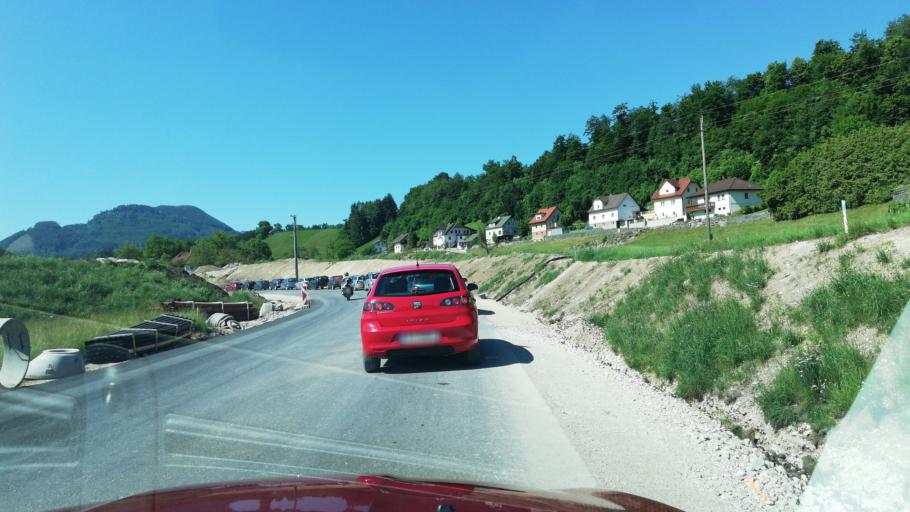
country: AT
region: Upper Austria
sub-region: Politischer Bezirk Kirchdorf an der Krems
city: Gruenburg
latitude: 47.9599
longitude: 14.2546
